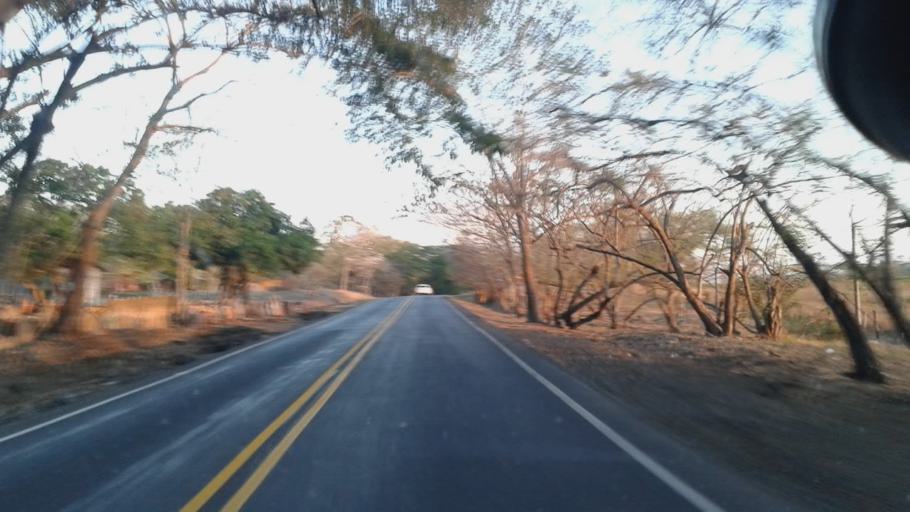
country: CR
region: Guanacaste
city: Juntas
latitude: 10.1470
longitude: -84.9106
